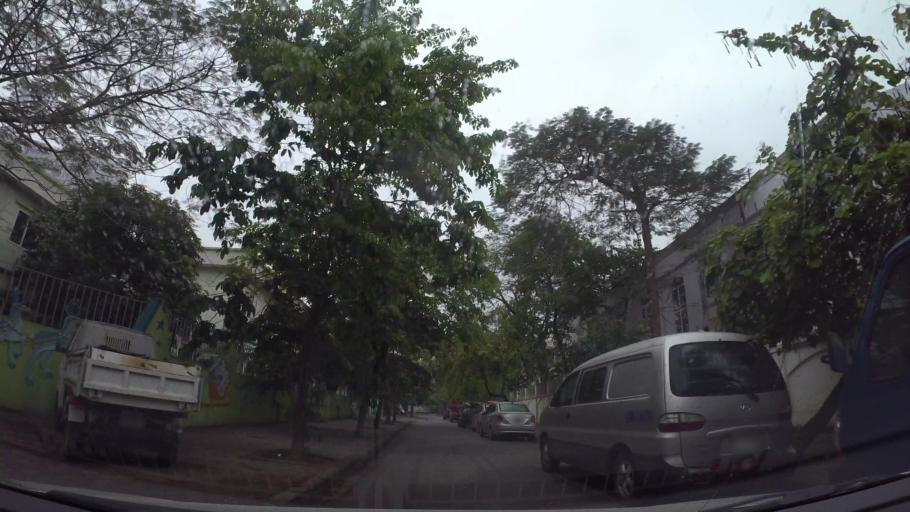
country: VN
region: Ha Noi
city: Cau Giay
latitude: 21.0146
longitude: 105.7984
